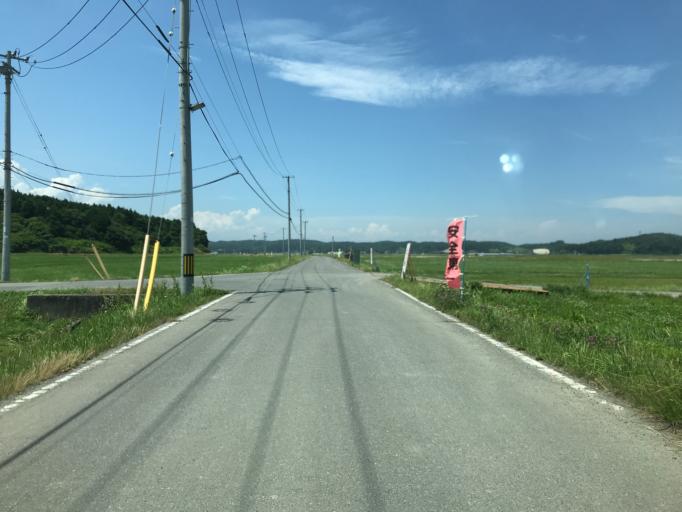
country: JP
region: Fukushima
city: Namie
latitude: 37.7244
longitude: 140.9949
